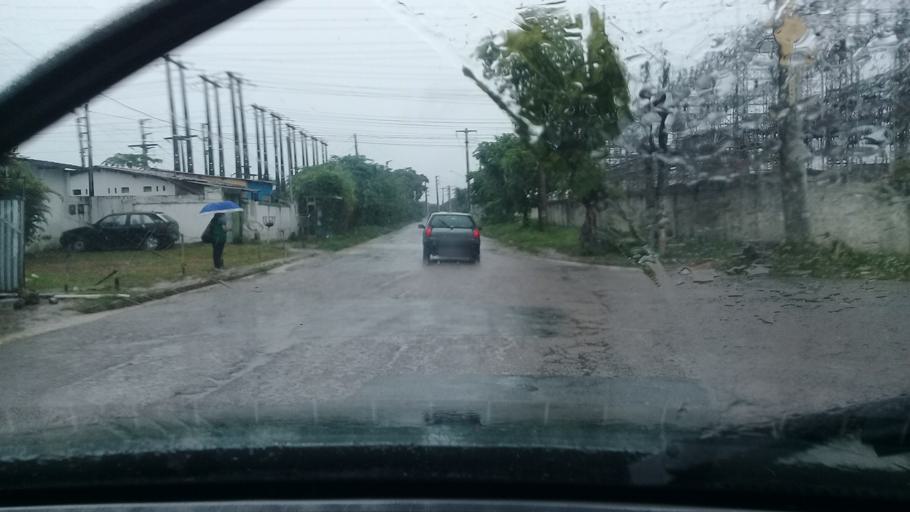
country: BR
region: Pernambuco
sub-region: Paulista
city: Paulista
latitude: -7.9547
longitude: -34.8903
